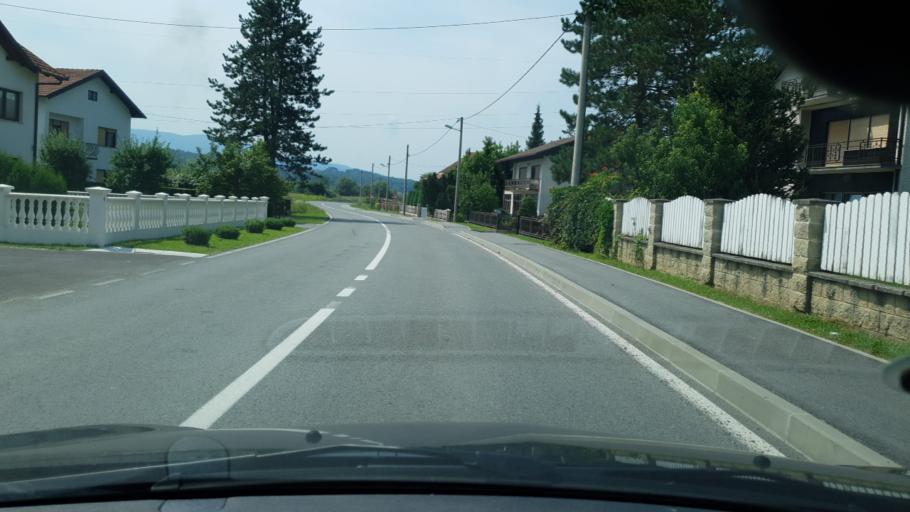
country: HR
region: Krapinsko-Zagorska
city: Bedekovcina
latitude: 46.0250
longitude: 15.9594
